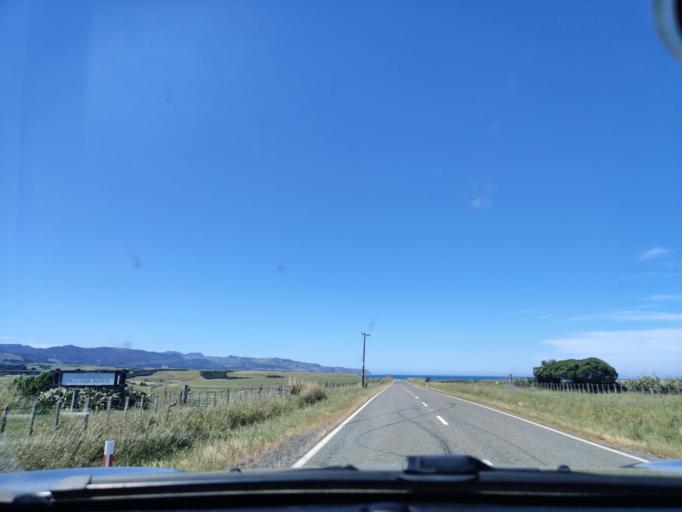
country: NZ
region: Wellington
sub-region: Upper Hutt City
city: Upper Hutt
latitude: -41.3934
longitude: 175.1763
